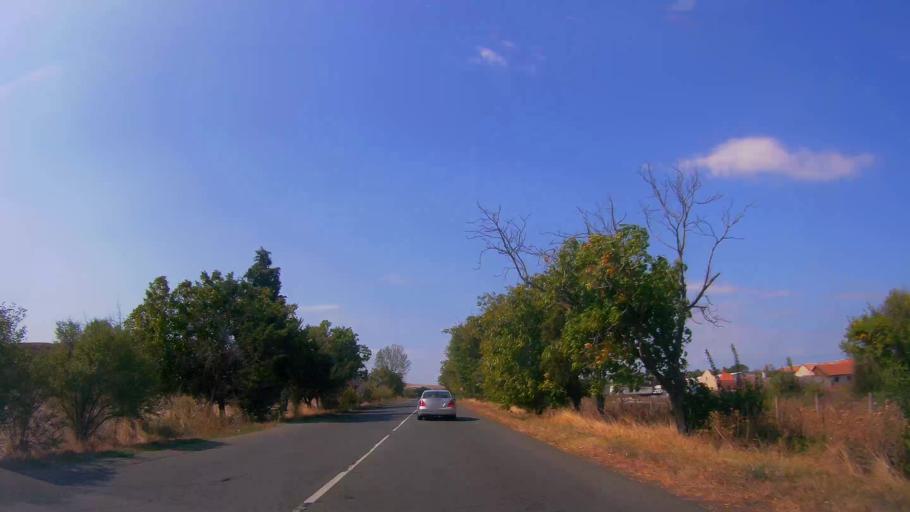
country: BG
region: Burgas
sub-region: Obshtina Karnobat
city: Karnobat
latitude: 42.6560
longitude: 27.0135
